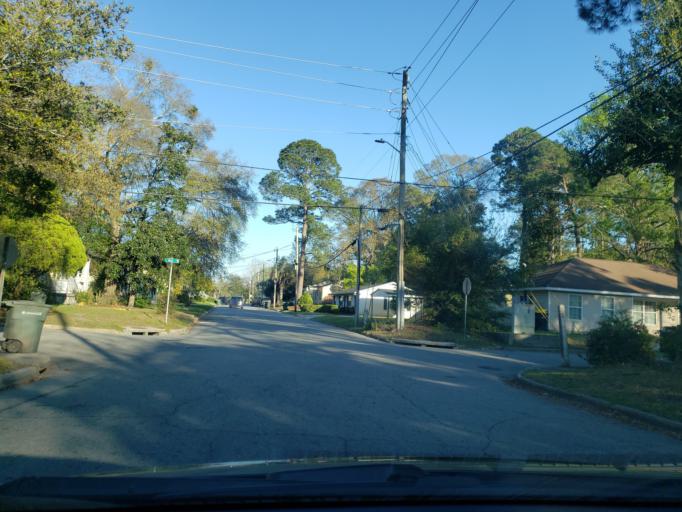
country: US
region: Georgia
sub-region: Chatham County
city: Thunderbolt
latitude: 32.0546
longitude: -81.0611
